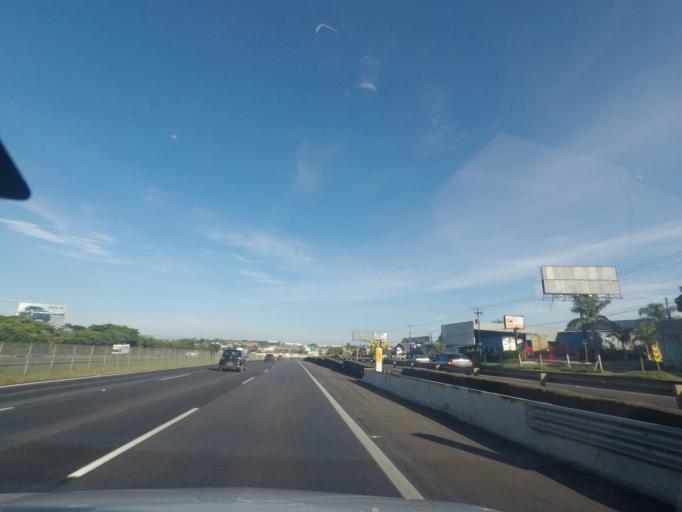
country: BR
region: Sao Paulo
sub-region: Hortolandia
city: Hortolandia
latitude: -22.8228
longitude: -47.1924
